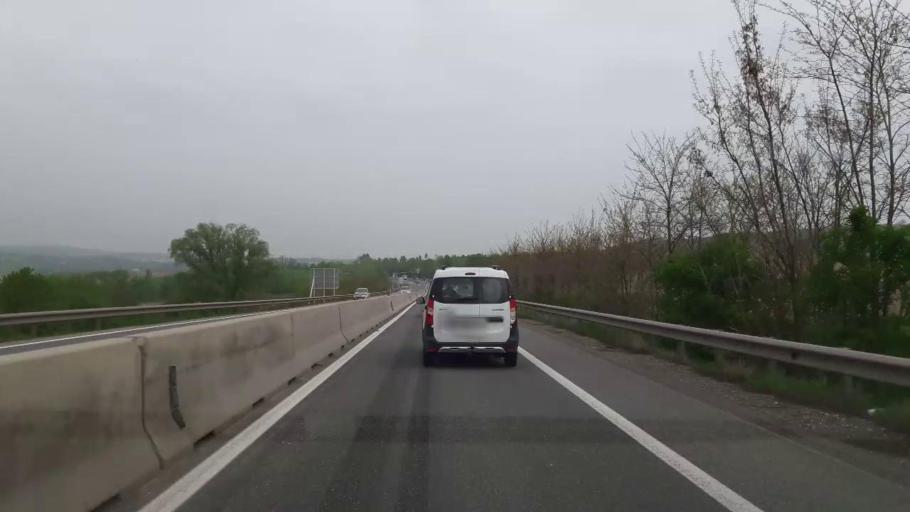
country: AT
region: Lower Austria
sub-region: Politischer Bezirk Hollabrunn
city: Hollabrunn
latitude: 48.5387
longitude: 16.0805
